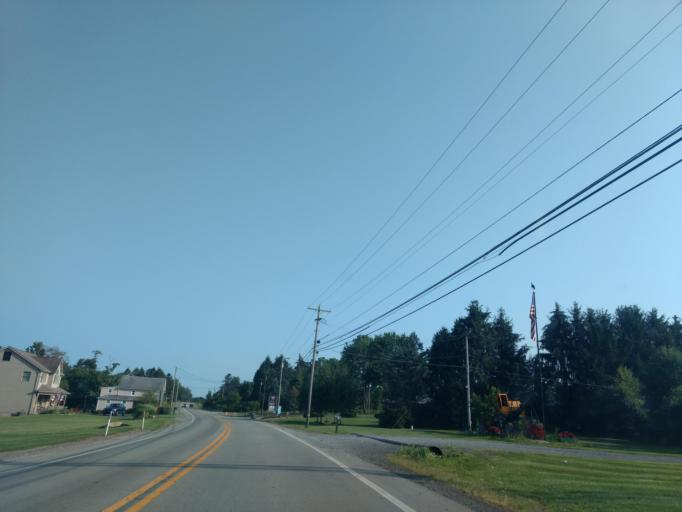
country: US
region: Pennsylvania
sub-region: Butler County
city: Zelienople
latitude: 40.8441
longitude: -80.1221
